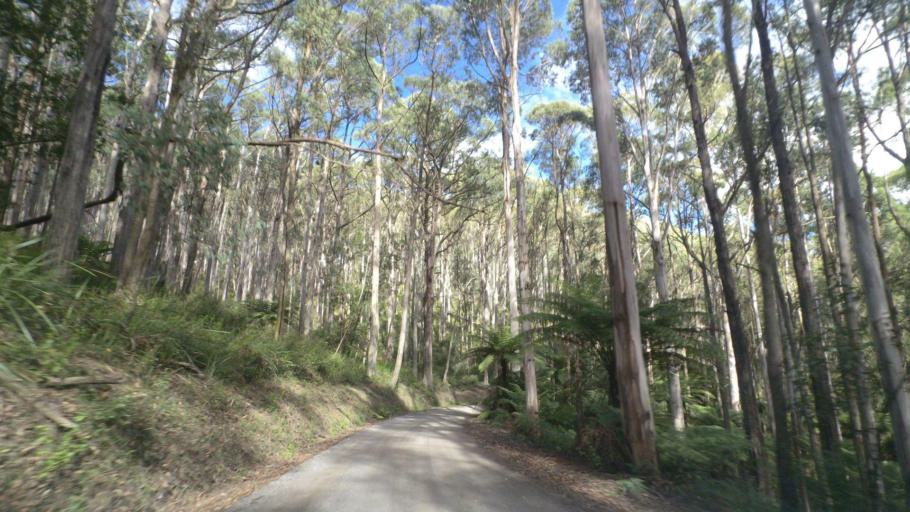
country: AU
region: Victoria
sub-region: Cardinia
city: Gembrook
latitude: -37.9200
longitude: 145.6025
